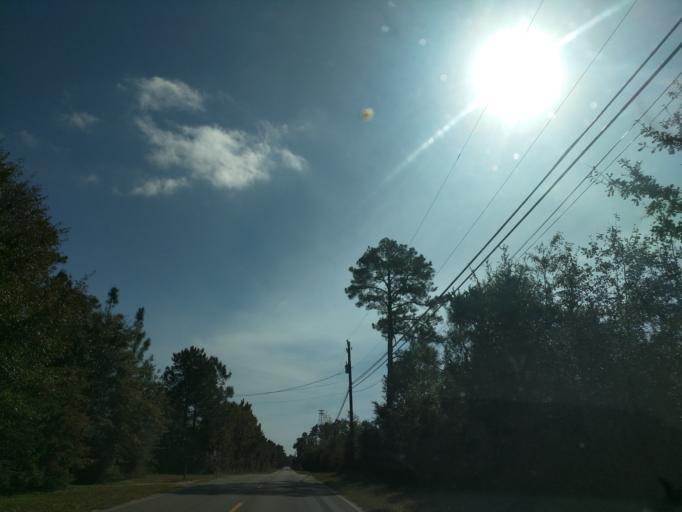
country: US
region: Florida
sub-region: Escambia County
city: Cantonment
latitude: 30.5447
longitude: -87.4059
